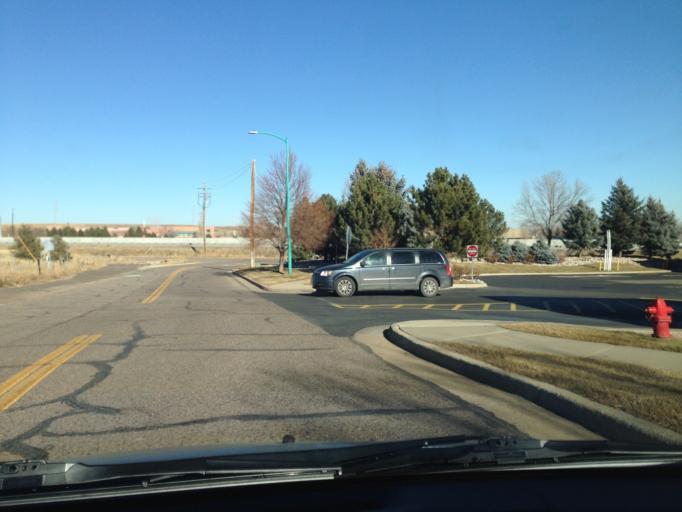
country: US
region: Colorado
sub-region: Boulder County
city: Superior
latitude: 39.9600
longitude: -105.1752
